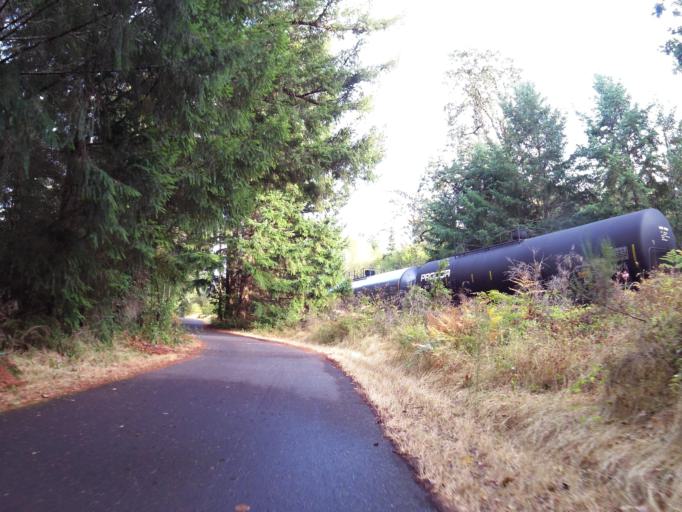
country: US
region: Washington
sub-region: Thurston County
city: Tenino
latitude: 46.9079
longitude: -122.7783
